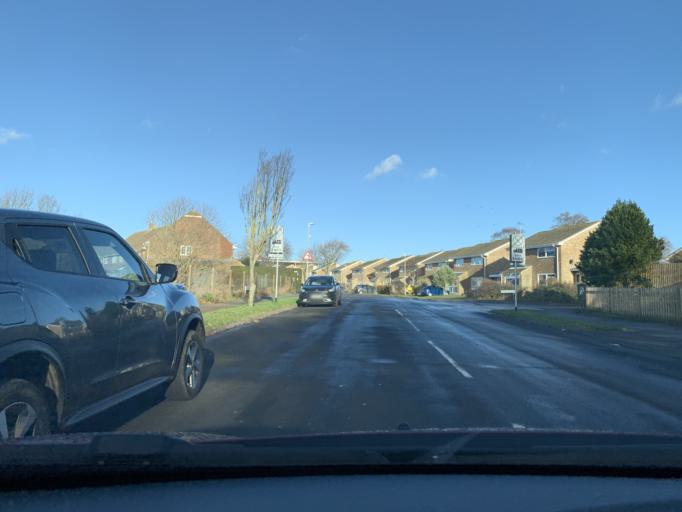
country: GB
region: England
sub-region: Kent
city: Folkestone
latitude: 51.0887
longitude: 1.1640
